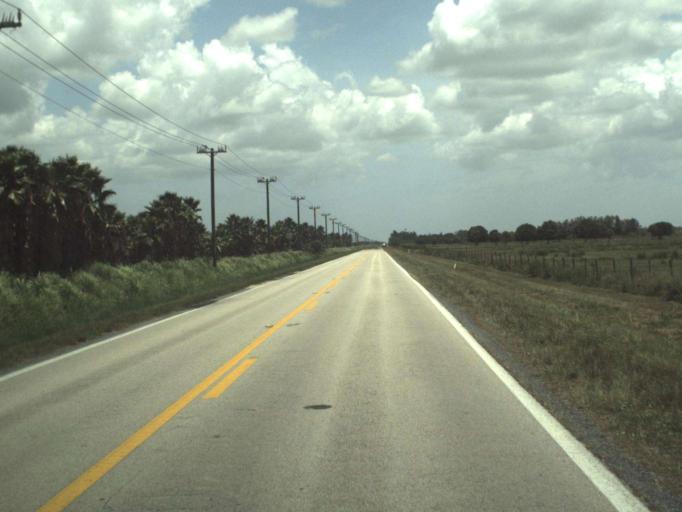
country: US
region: Florida
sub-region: Saint Lucie County
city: Fort Pierce South
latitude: 27.3744
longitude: -80.4802
